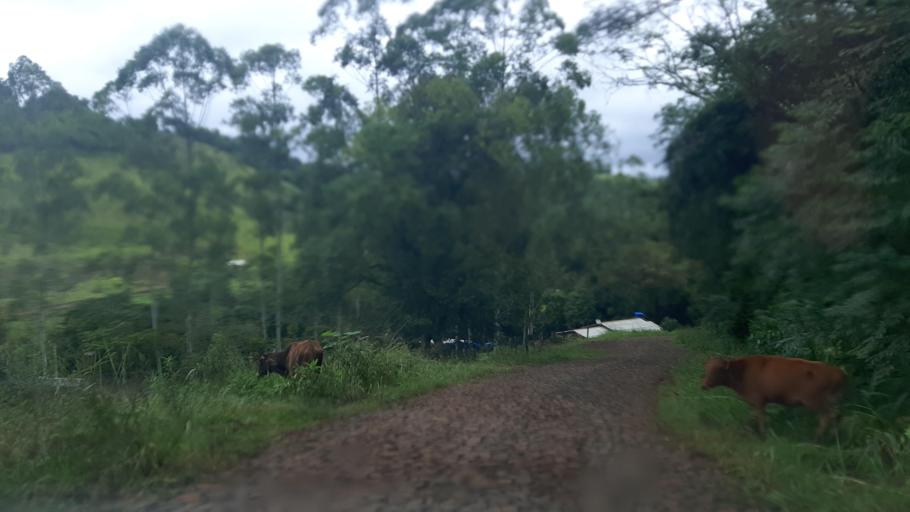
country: BR
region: Parana
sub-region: Ampere
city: Ampere
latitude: -26.0456
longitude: -53.5154
